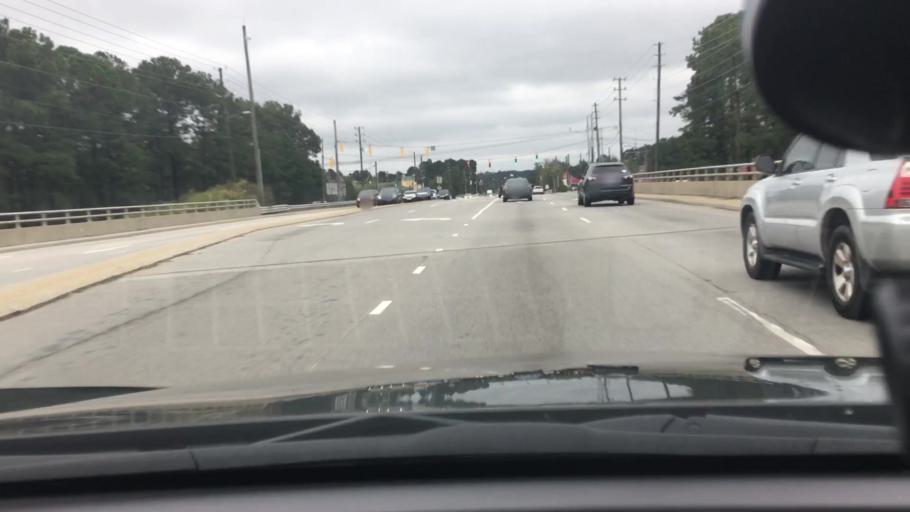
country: US
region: North Carolina
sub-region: Wake County
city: Apex
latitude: 35.7147
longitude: -78.8405
